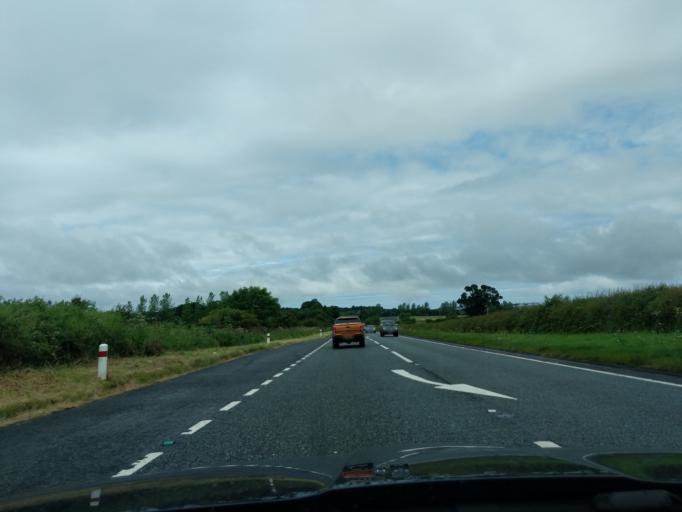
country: GB
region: England
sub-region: Northumberland
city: Belford
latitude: 55.5849
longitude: -1.8084
